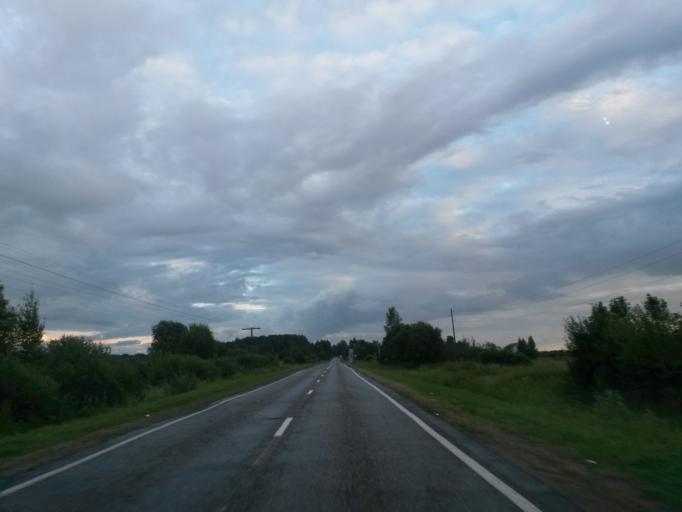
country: RU
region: Jaroslavl
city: Tutayev
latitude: 57.9030
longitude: 39.5234
